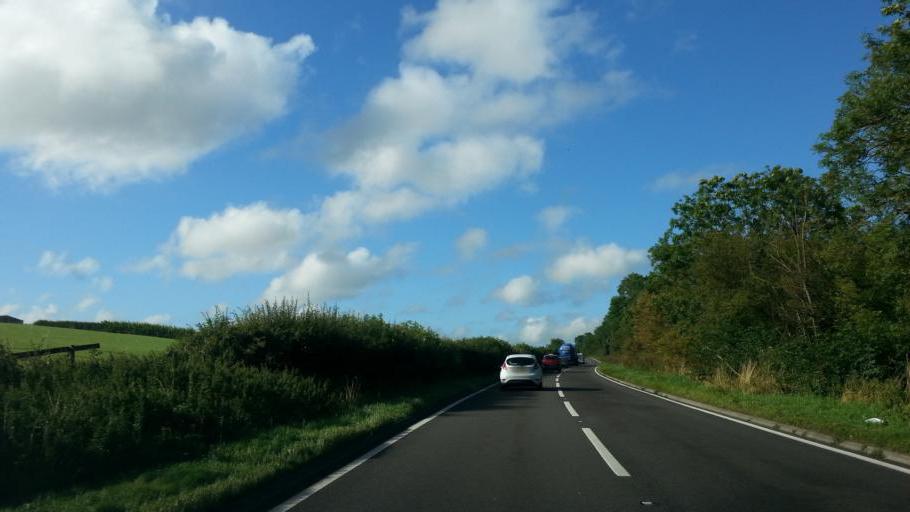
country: GB
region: England
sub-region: District of Rutland
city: South Luffenham
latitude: 52.5509
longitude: -0.5809
